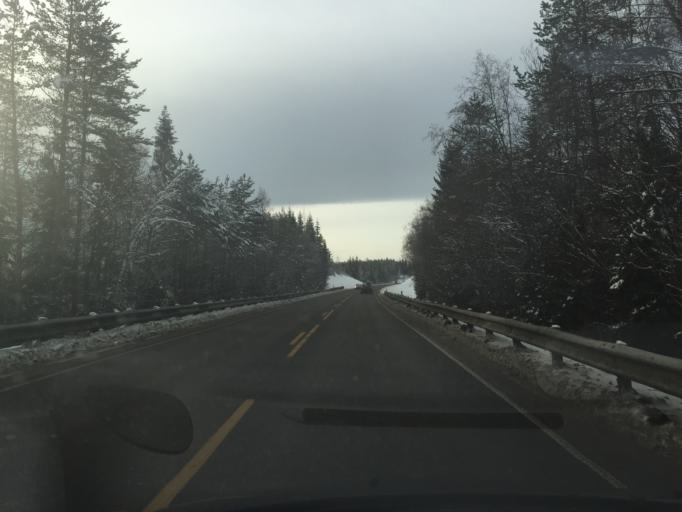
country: NO
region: Hedmark
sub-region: Elverum
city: Elverum
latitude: 60.9490
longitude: 11.6963
